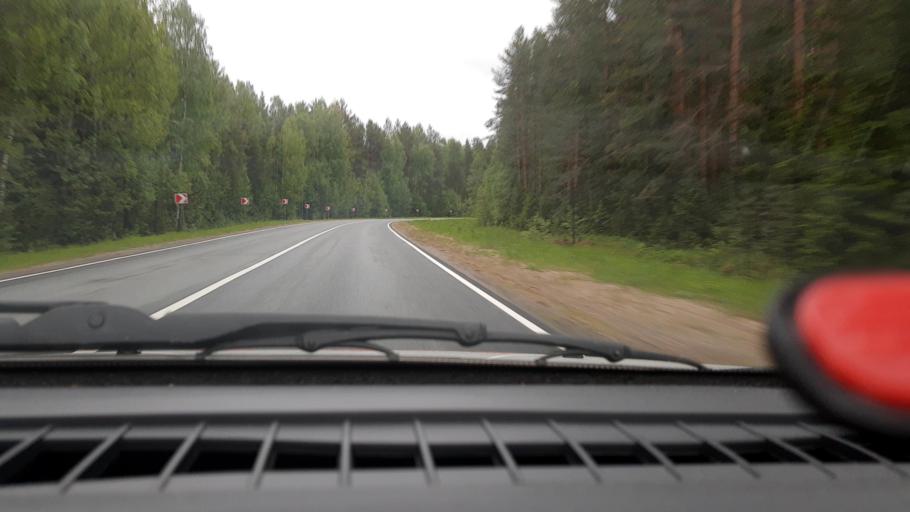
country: RU
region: Nizjnij Novgorod
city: Krasnyye Baki
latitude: 57.2239
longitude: 45.4887
